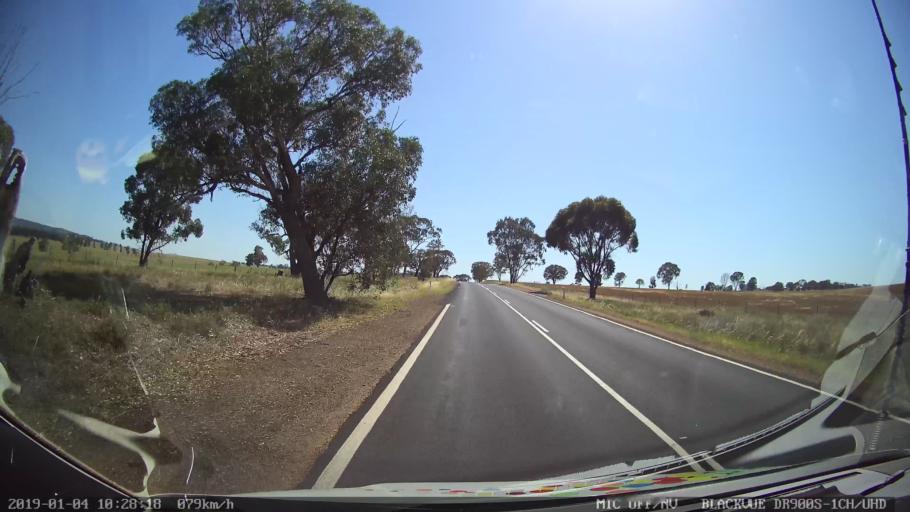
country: AU
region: New South Wales
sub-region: Cabonne
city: Canowindra
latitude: -33.3642
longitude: 148.6080
